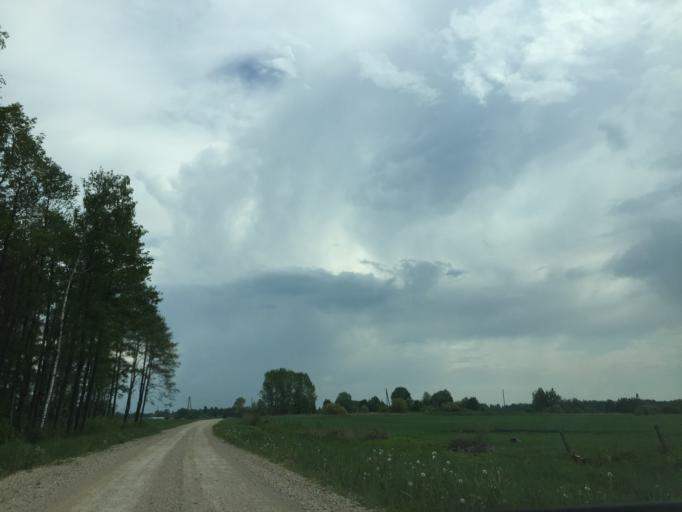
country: LV
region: Livani
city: Livani
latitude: 56.5526
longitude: 26.2277
